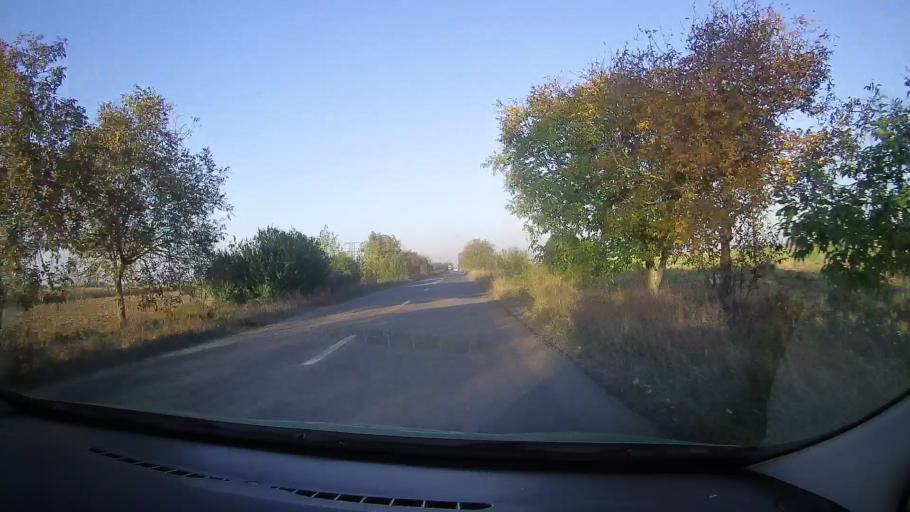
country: RO
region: Bihor
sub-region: Comuna Biharea
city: Biharea
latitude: 47.1685
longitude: 21.9535
